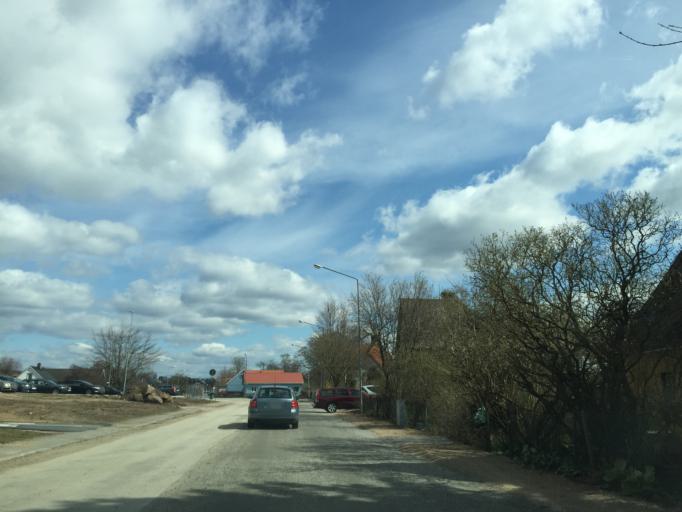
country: SE
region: Skane
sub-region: Horby Kommun
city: Hoerby
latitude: 55.8582
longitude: 13.6583
